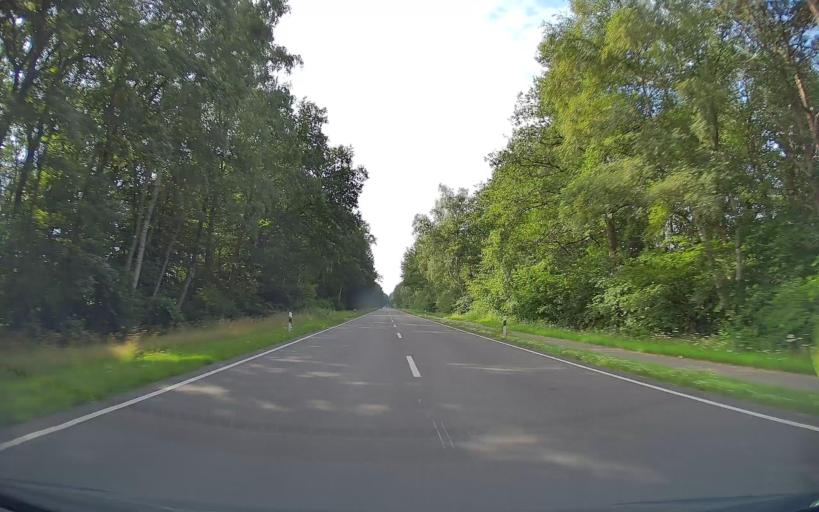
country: DE
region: Lower Saxony
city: Molbergen
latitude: 52.9312
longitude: 7.9482
